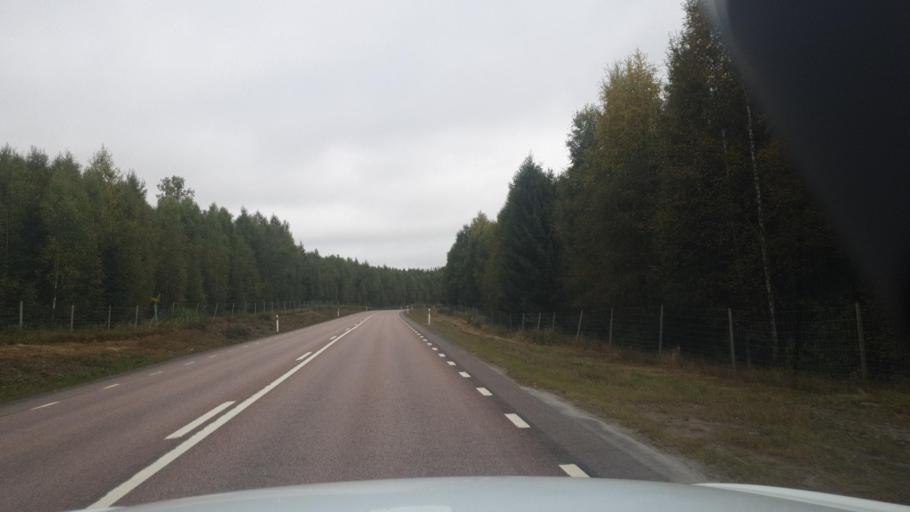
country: SE
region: Vaermland
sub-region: Sunne Kommun
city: Sunne
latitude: 59.7686
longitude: 13.1020
